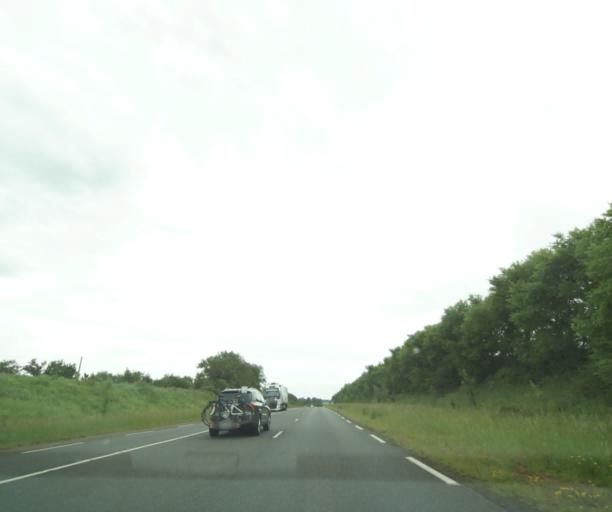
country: FR
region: Poitou-Charentes
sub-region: Departement des Deux-Sevres
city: Airvault
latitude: 46.8038
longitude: -0.2120
